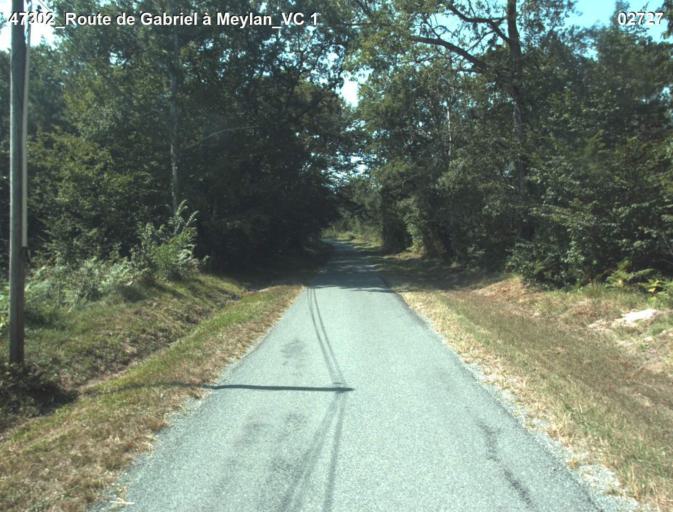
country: FR
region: Aquitaine
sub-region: Departement du Lot-et-Garonne
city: Mezin
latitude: 44.0717
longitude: 0.1304
